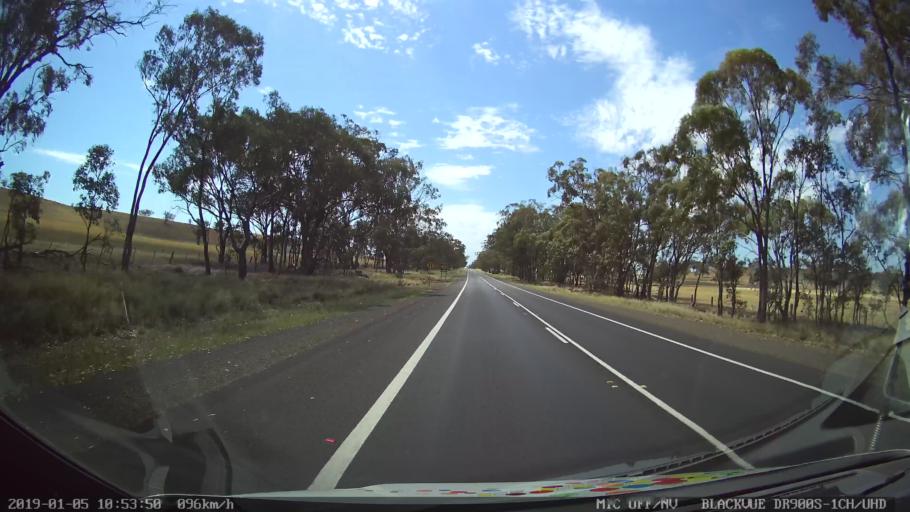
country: AU
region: New South Wales
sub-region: Warrumbungle Shire
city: Coonabarabran
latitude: -31.4452
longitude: 149.1199
